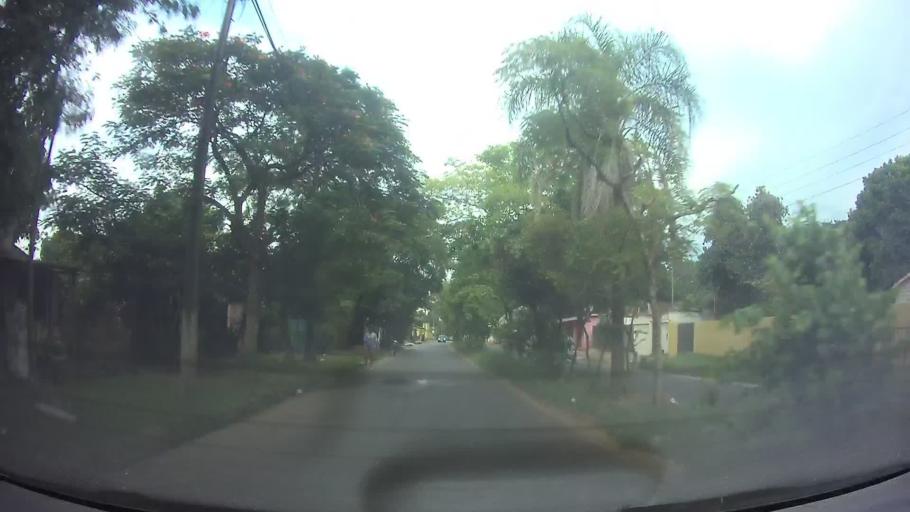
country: PY
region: Central
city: San Lorenzo
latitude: -25.2711
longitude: -57.4804
